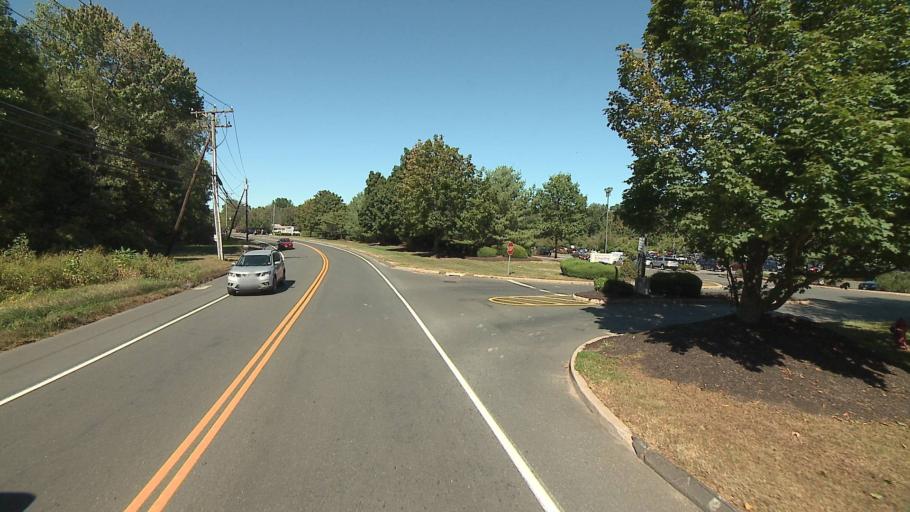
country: US
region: Connecticut
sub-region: Hartford County
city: Salmon Brook
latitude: 41.9348
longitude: -72.7903
